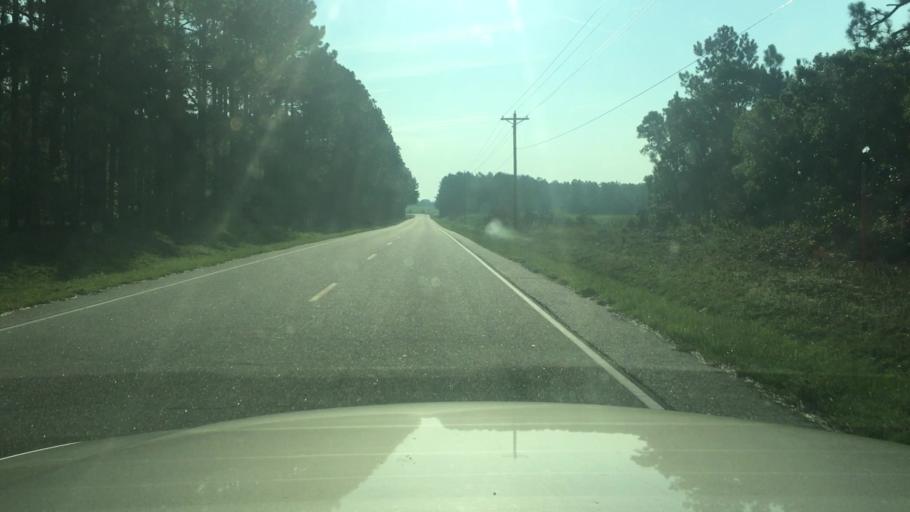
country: US
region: North Carolina
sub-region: Harnett County
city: Walkertown
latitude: 35.2082
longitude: -78.8624
